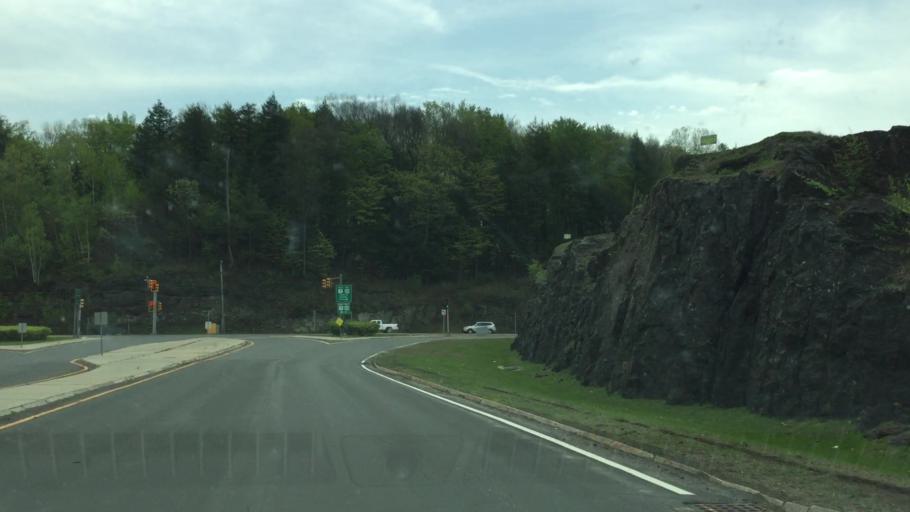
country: US
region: Massachusetts
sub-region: Berkshire County
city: Pittsfield
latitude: 42.4106
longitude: -73.2640
